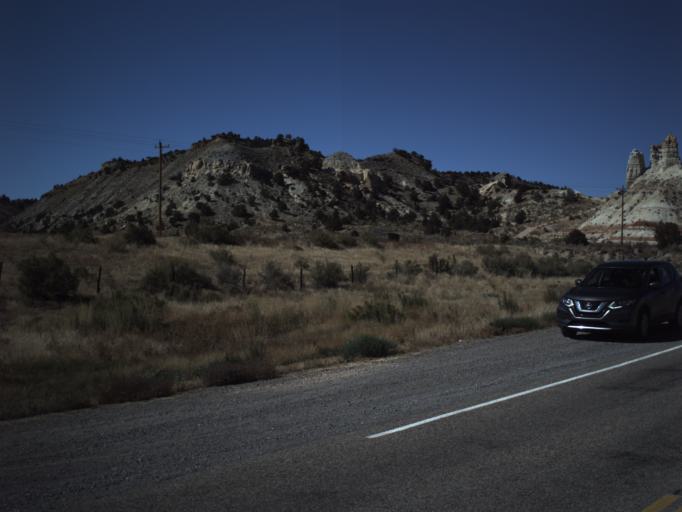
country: US
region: Utah
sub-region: Garfield County
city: Panguitch
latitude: 37.5841
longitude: -112.0573
